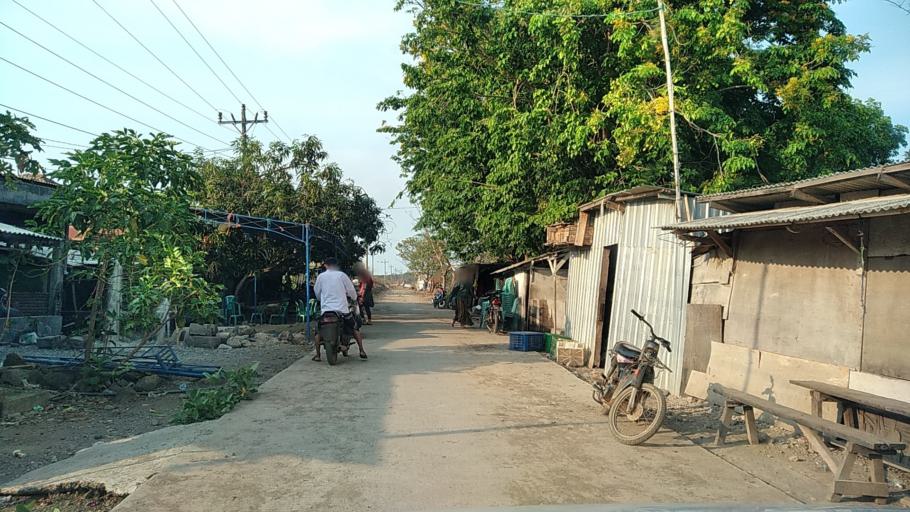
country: ID
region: Central Java
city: Semarang
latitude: -6.9512
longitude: 110.3065
